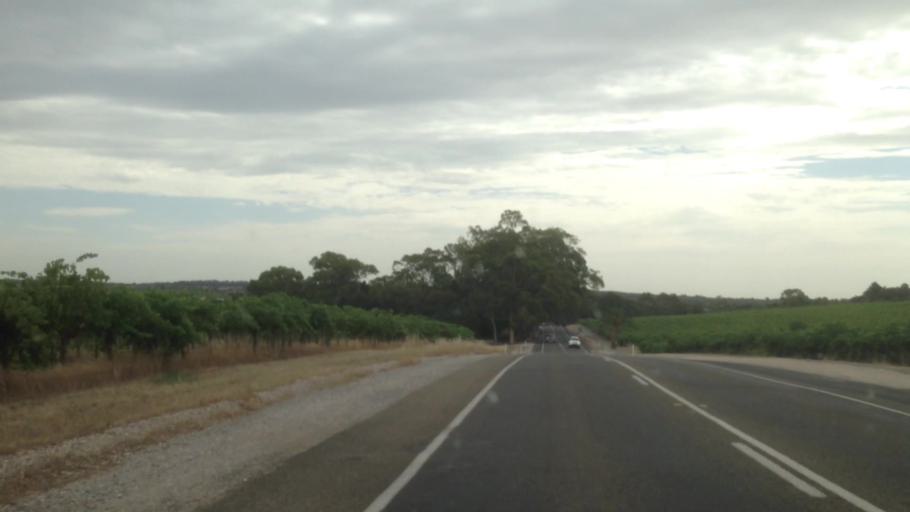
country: AU
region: South Australia
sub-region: Barossa
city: Lyndoch
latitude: -34.5974
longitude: 138.9122
